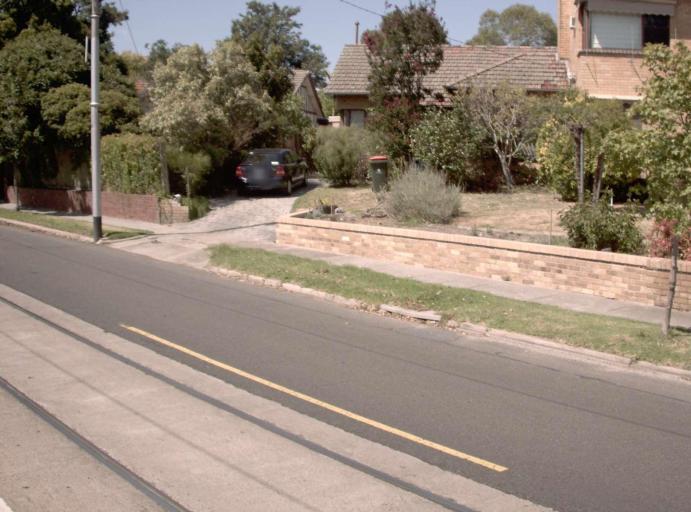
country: AU
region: Victoria
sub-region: Boroondara
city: Camberwell
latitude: -37.8437
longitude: 145.0709
